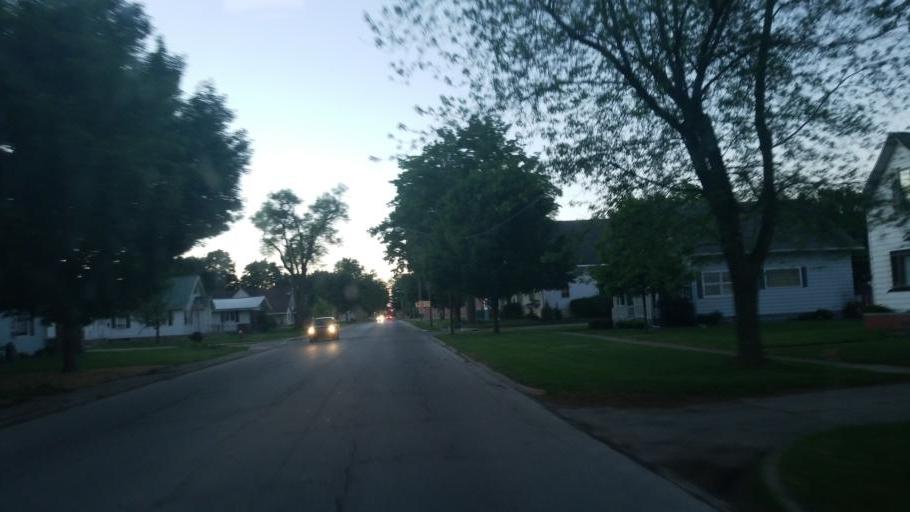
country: US
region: Indiana
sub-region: Elkhart County
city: Nappanee
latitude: 41.4366
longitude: -86.0014
